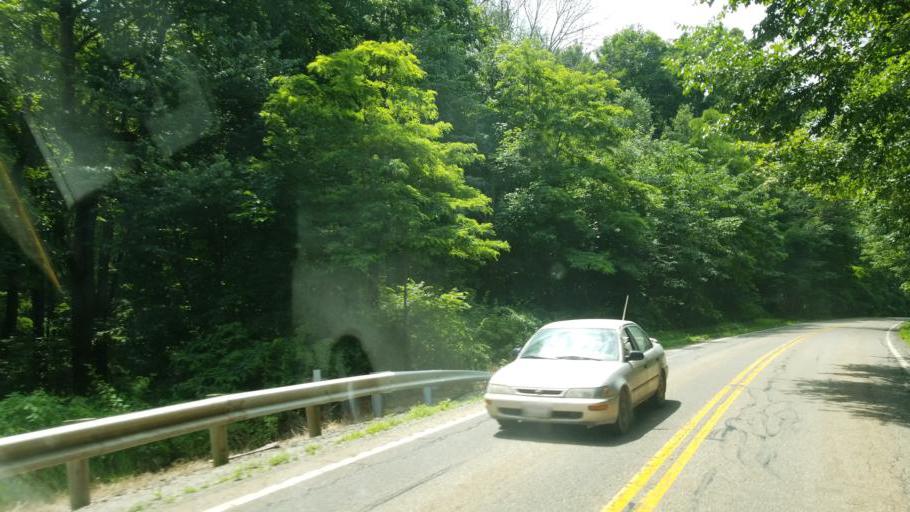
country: US
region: Ohio
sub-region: Mahoning County
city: Sebring
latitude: 40.7890
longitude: -80.9736
